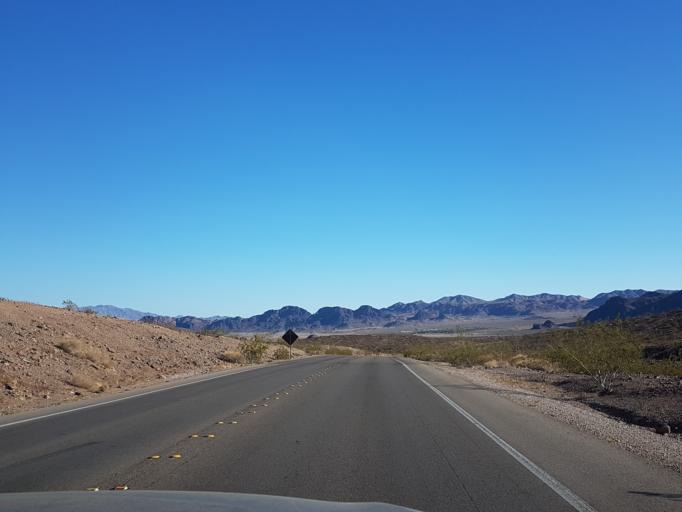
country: US
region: Nevada
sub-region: Clark County
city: Boulder City
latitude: 36.0754
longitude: -114.8212
